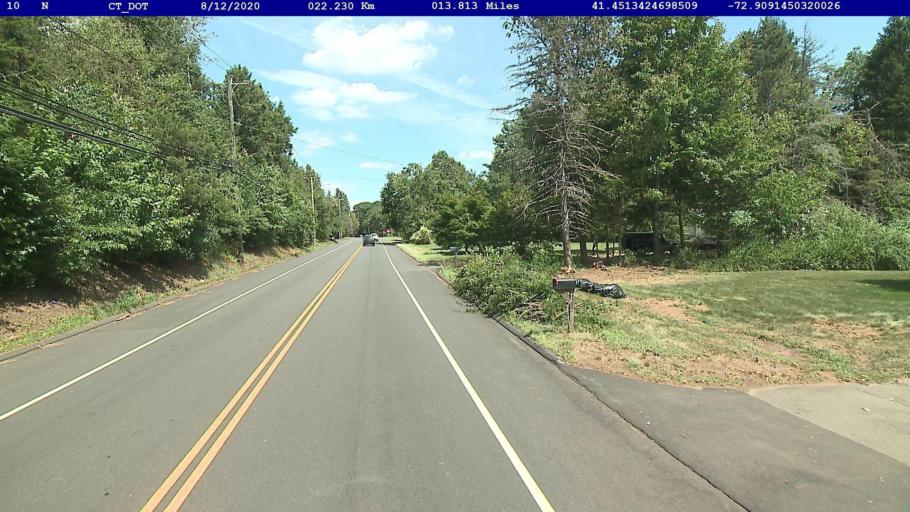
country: US
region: Connecticut
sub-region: New Haven County
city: Cheshire
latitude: 41.4513
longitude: -72.9091
